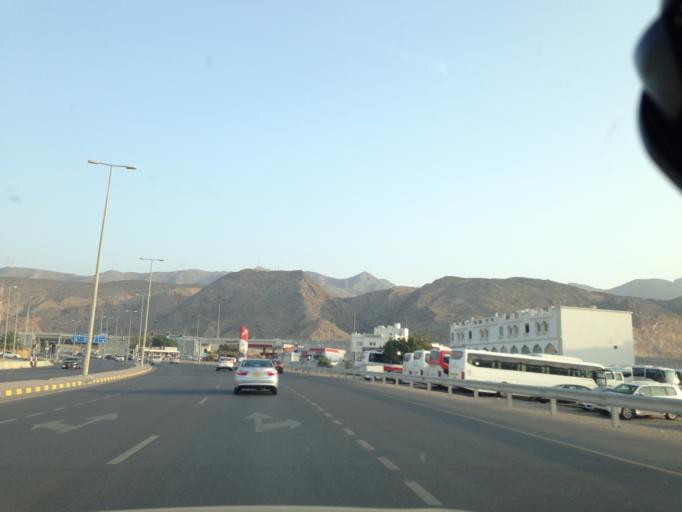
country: OM
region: Muhafazat Masqat
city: Bawshar
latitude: 23.5930
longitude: 58.4580
